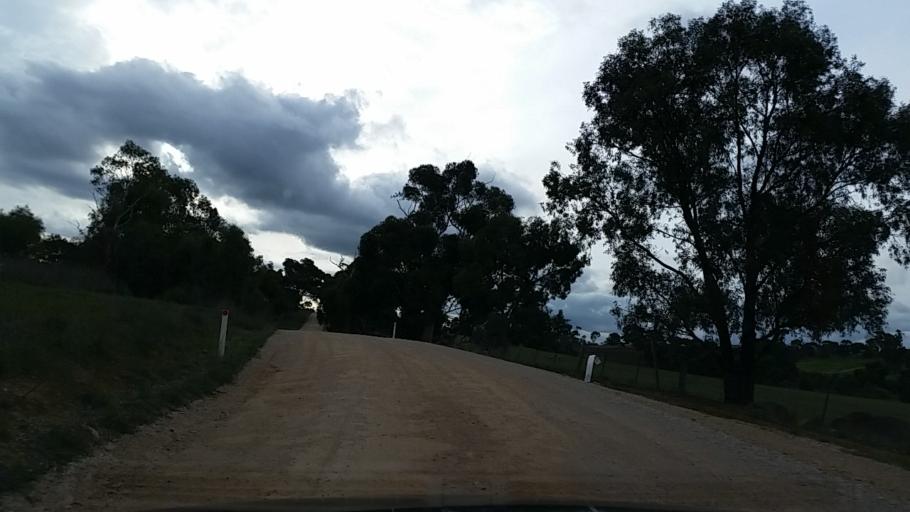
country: AU
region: South Australia
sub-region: Mount Barker
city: Nairne
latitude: -34.9824
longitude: 139.0371
